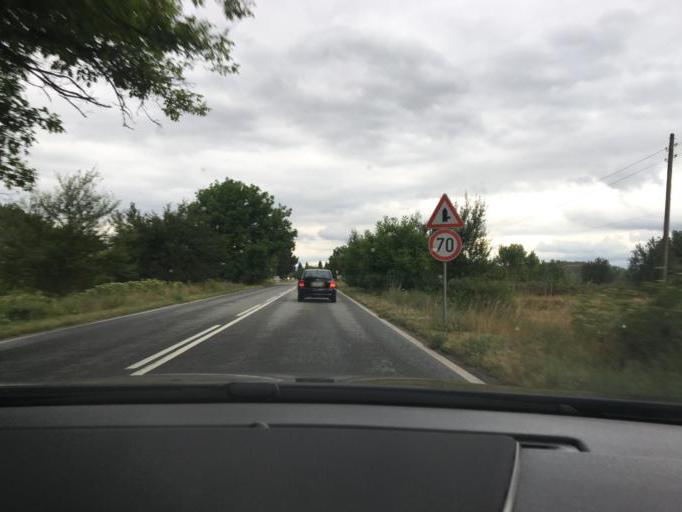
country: BG
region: Kyustendil
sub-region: Obshtina Kyustendil
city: Kyustendil
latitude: 42.2599
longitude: 22.8338
